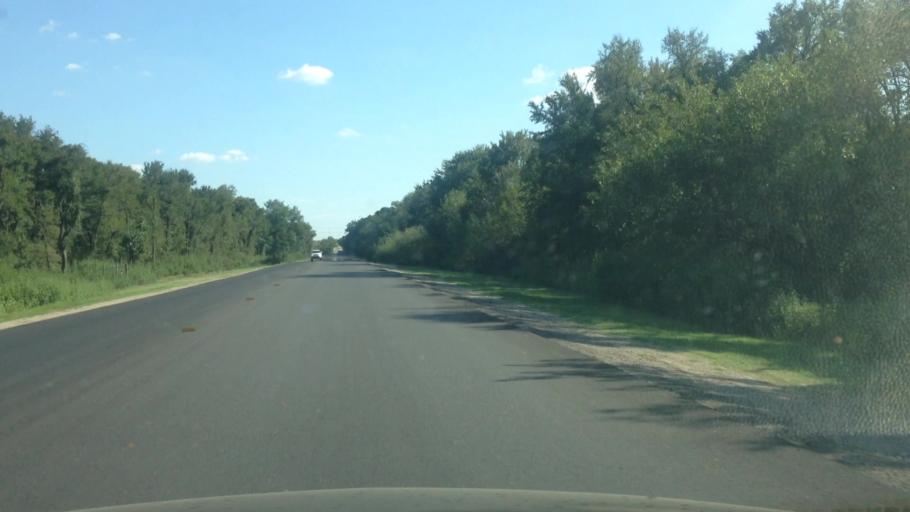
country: US
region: Texas
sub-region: Dallas County
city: Irving
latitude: 32.8625
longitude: -96.9163
